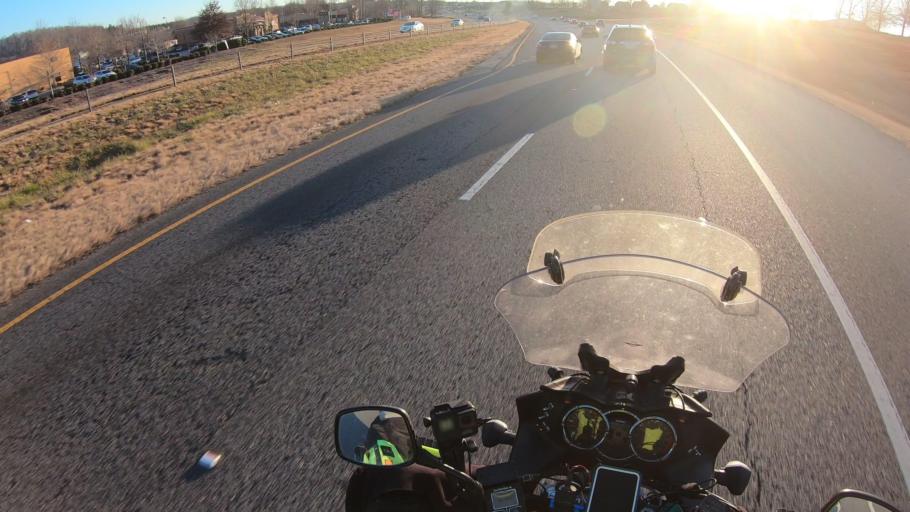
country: US
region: Georgia
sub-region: Dawson County
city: Dawsonville
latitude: 34.3563
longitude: -84.0435
